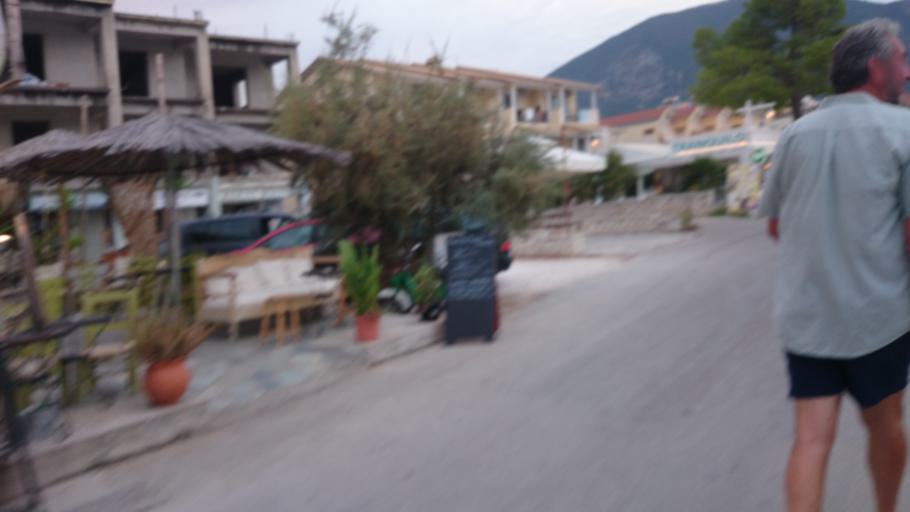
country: GR
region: Ionian Islands
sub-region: Lefkada
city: Nidri
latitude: 38.7041
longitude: 20.7087
